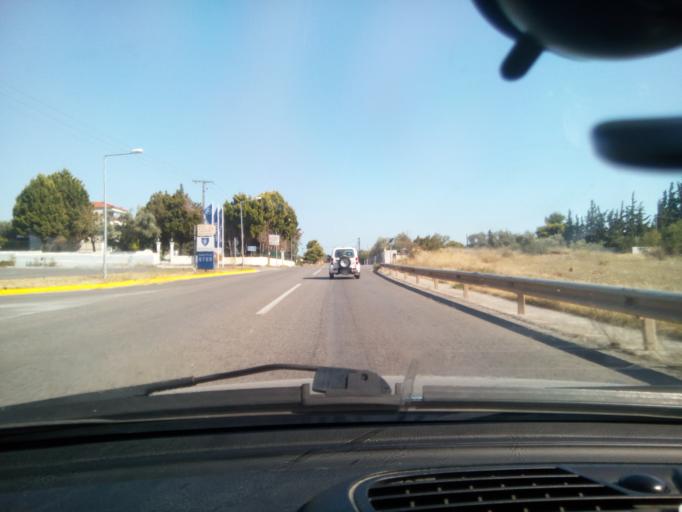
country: GR
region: Central Greece
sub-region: Nomos Evvoias
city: Malakonta
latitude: 38.4090
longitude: 23.7275
